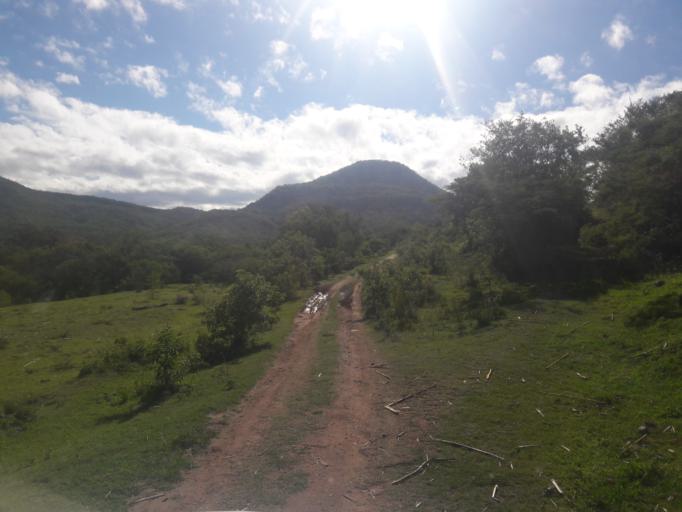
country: MX
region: Oaxaca
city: Ciudad de Huajuapam de Leon
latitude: 17.8426
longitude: -97.7888
